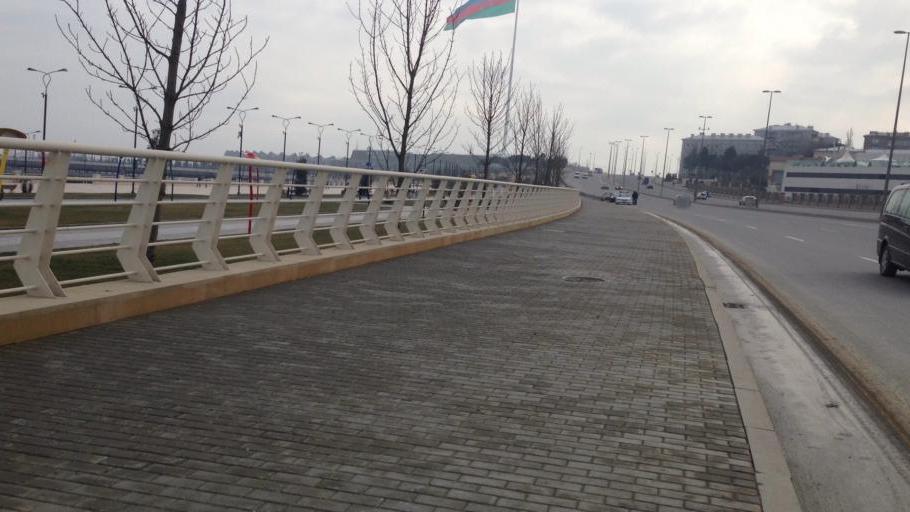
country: AZ
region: Baki
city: Badamdar
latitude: 40.3487
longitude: 49.8374
